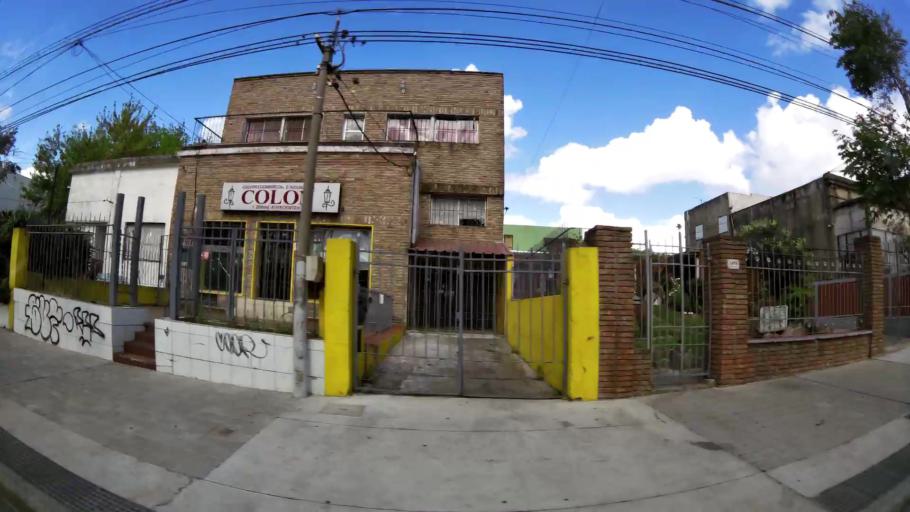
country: UY
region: Canelones
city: La Paz
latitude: -34.8182
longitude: -56.2201
